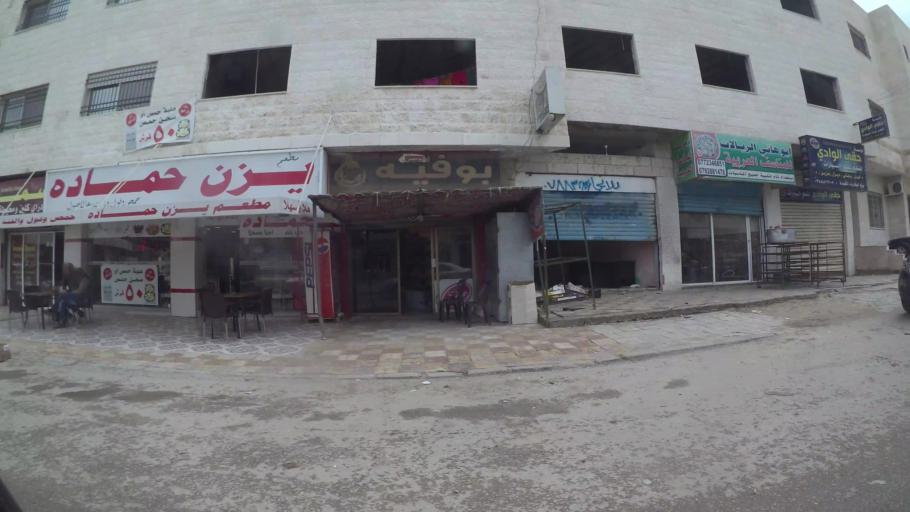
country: JO
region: Amman
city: Al Jubayhah
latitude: 32.0542
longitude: 35.8341
